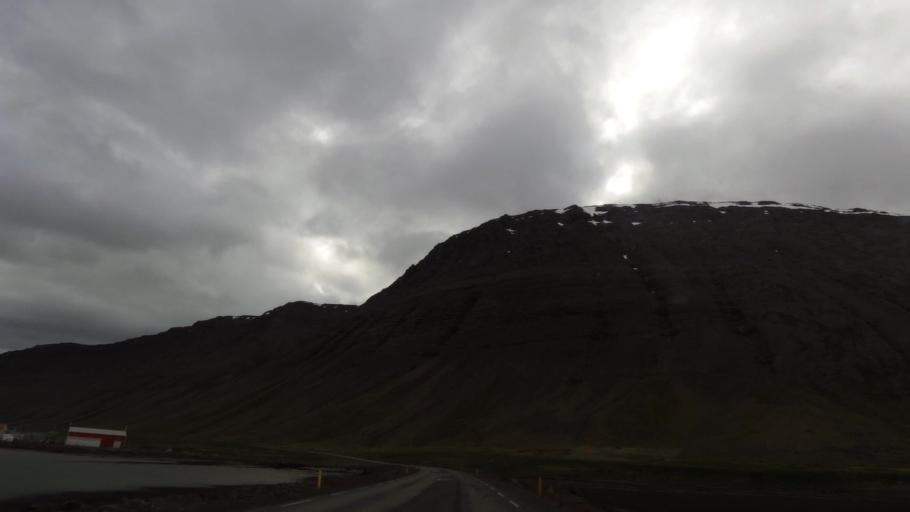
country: IS
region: Westfjords
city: Isafjoerdur
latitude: 66.0529
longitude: -23.1520
